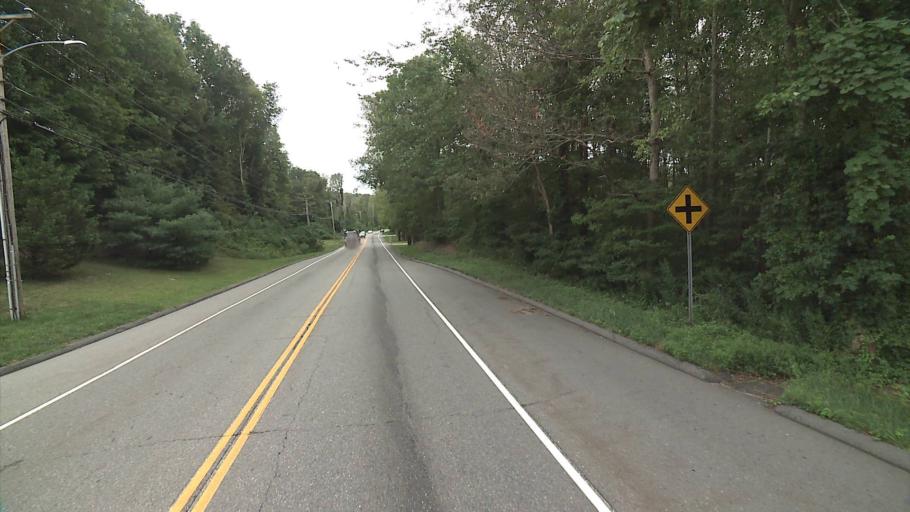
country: US
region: Connecticut
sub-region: New London County
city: Montville Center
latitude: 41.4437
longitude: -72.2302
